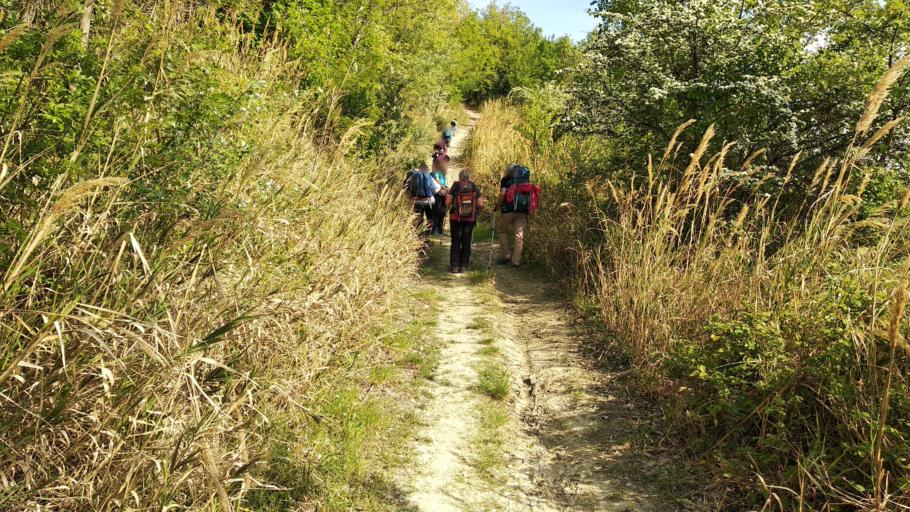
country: IT
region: Emilia-Romagna
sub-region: Provincia di Ravenna
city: Fognano
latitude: 44.2261
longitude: 11.7219
